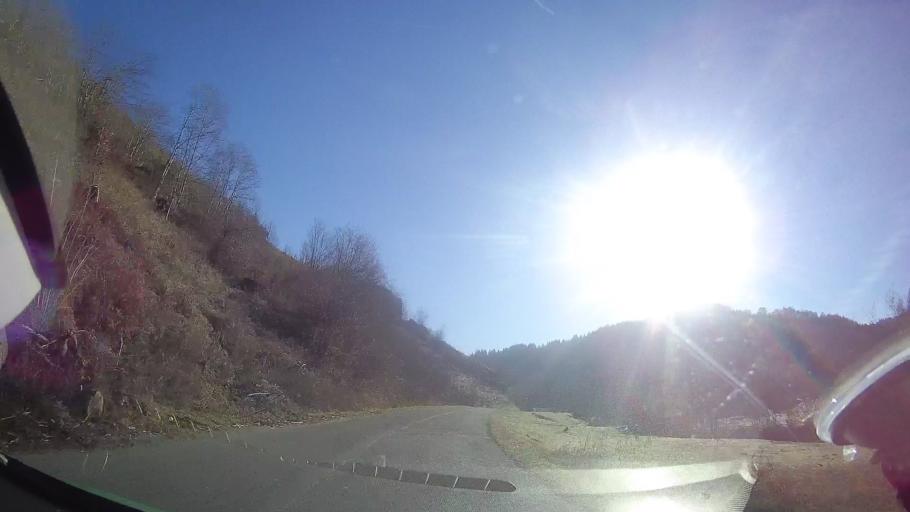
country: RO
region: Cluj
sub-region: Comuna Sacueu
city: Sacuieu
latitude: 46.8298
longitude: 22.8756
